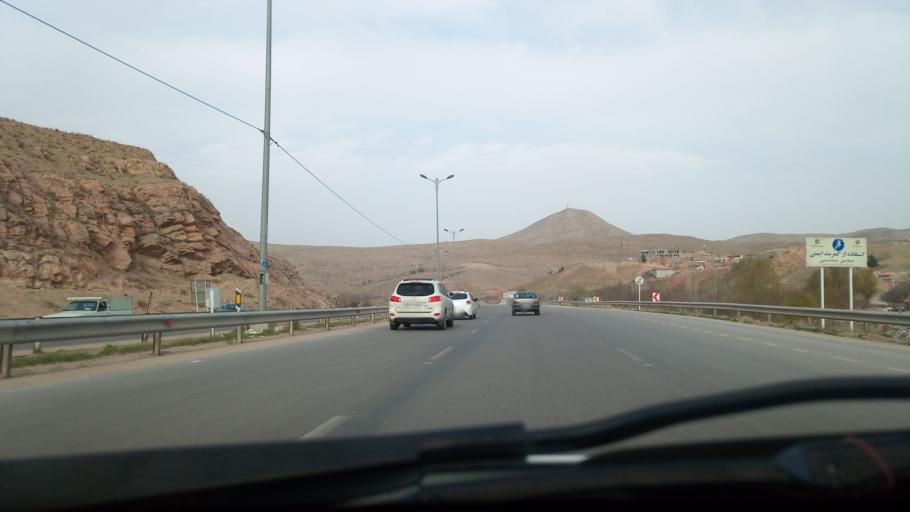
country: IR
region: Khorasan-e Shomali
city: Bojnurd
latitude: 37.4781
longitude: 57.4316
